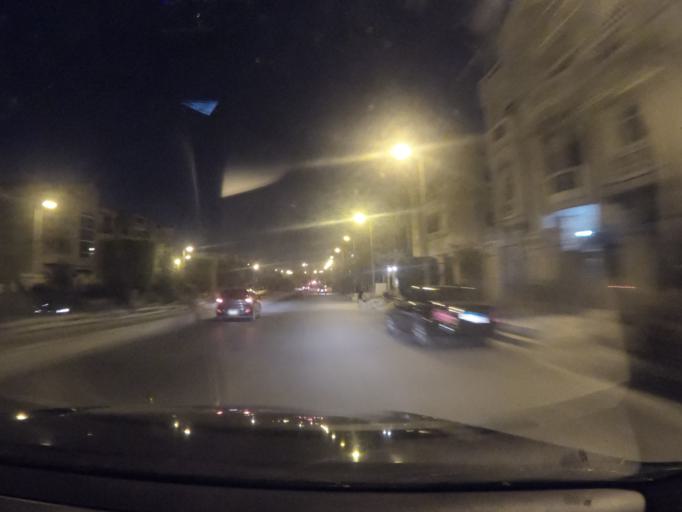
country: EG
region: Muhafazat al Qahirah
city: Cairo
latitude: 30.0126
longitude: 31.4188
